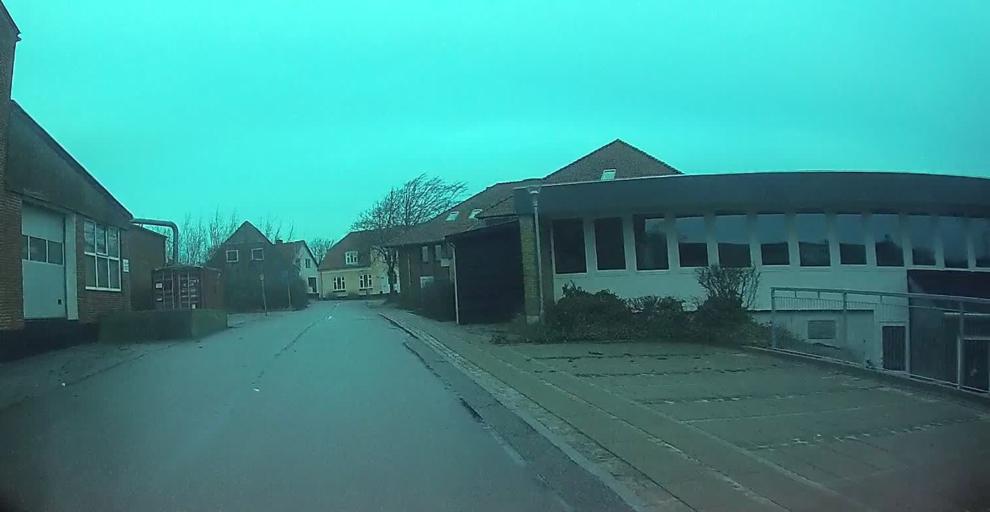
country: DK
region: North Denmark
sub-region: Thisted Kommune
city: Hurup
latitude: 56.7502
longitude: 8.4223
